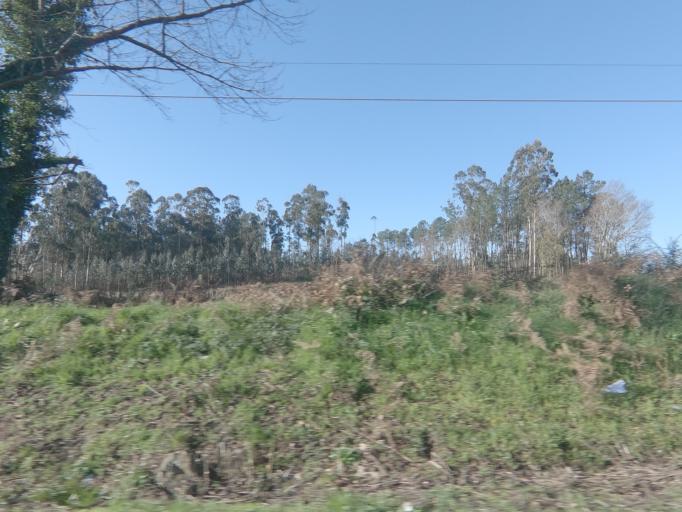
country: ES
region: Galicia
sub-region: Provincia da Coruna
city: Vedra
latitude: 42.8079
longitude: -8.4786
